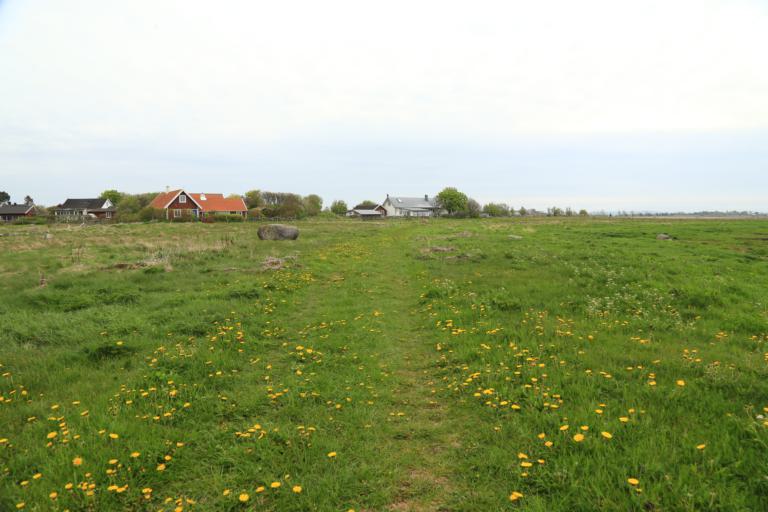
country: SE
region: Halland
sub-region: Varbergs Kommun
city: Traslovslage
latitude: 57.0252
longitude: 12.3171
